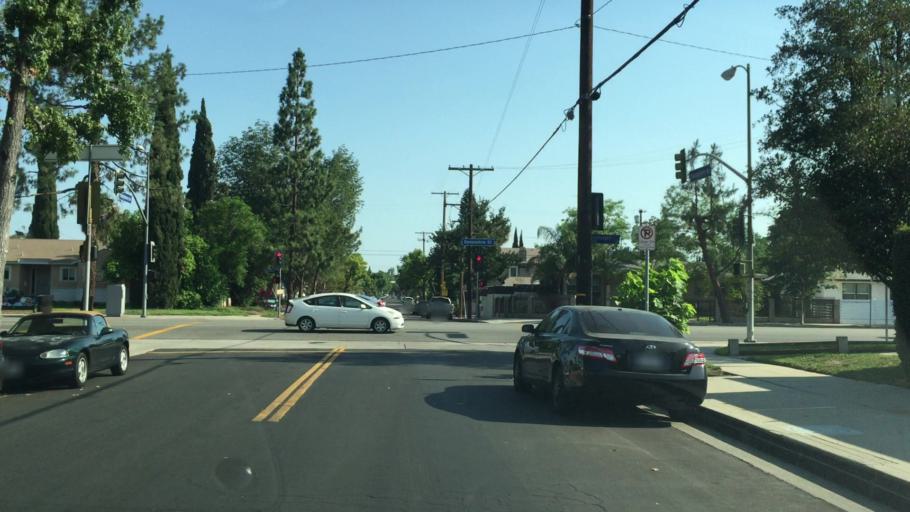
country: US
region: California
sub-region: Los Angeles County
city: San Fernando
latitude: 34.2578
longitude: -118.4817
